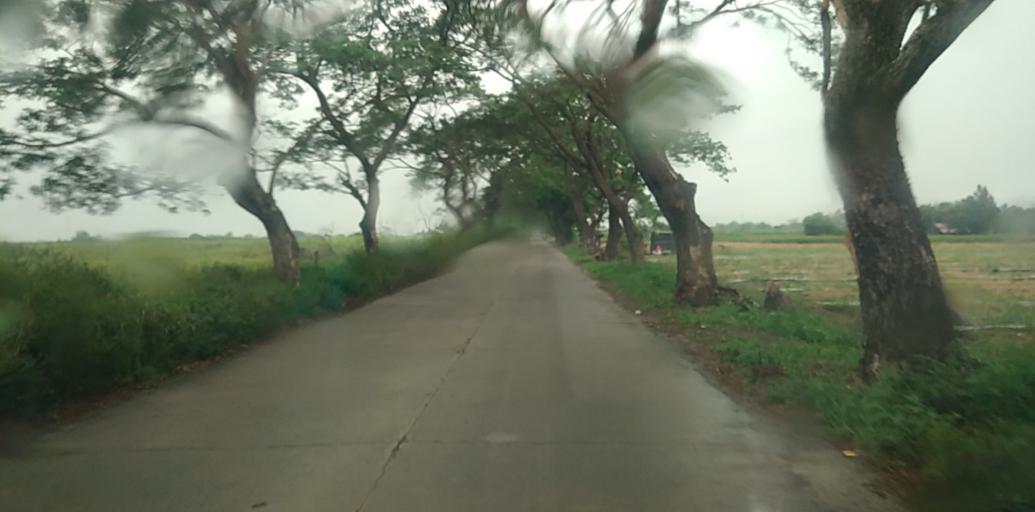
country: PH
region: Central Luzon
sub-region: Province of Pampanga
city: Anao
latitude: 15.1501
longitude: 120.7009
